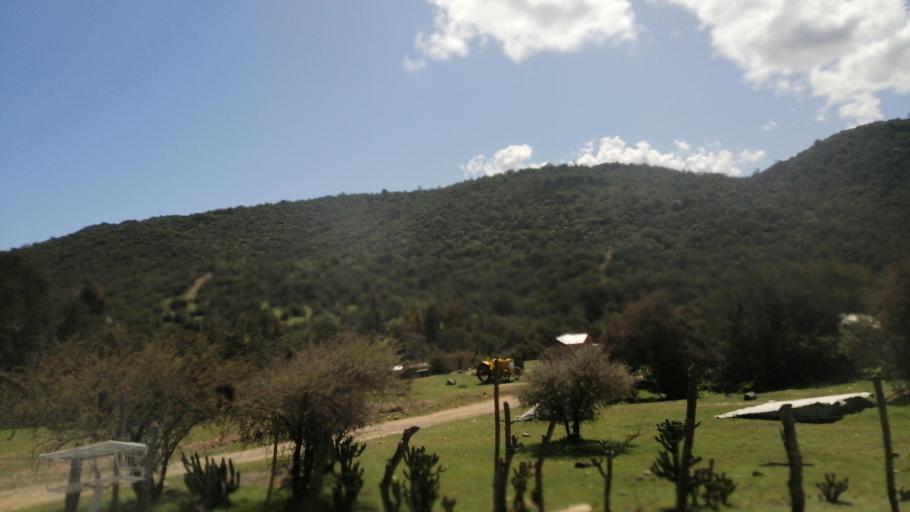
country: CL
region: Valparaiso
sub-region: Provincia de Marga Marga
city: Limache
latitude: -33.2041
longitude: -71.2492
